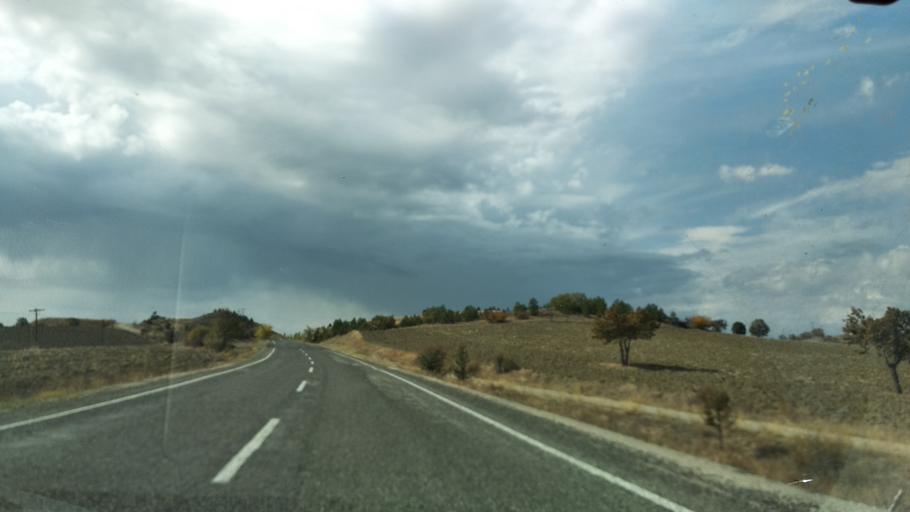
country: TR
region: Bolu
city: Seben
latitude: 40.3869
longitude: 31.5382
